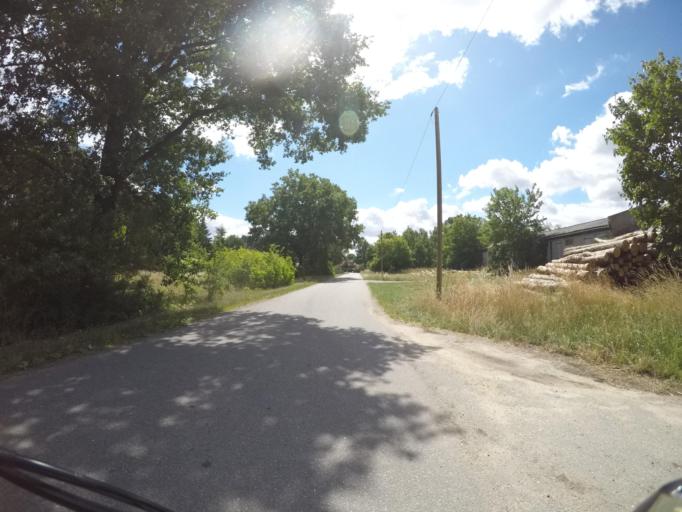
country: DE
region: Lower Saxony
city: Hitzacker
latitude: 53.2099
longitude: 11.0138
